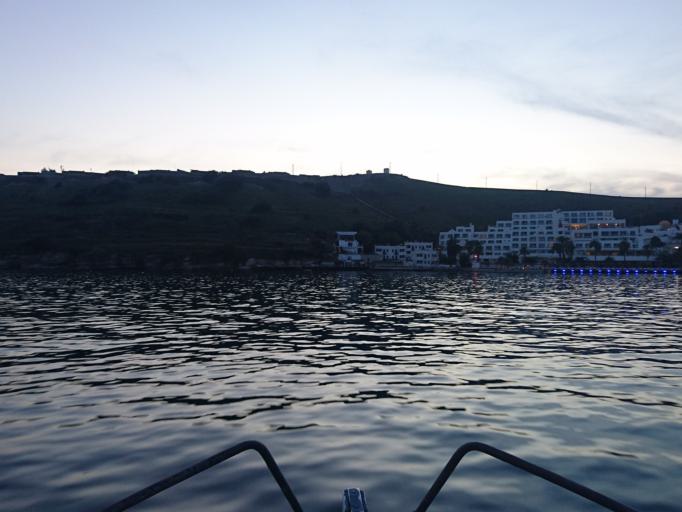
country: TR
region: Mugla
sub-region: Bodrum
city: Bodrum
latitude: 37.0278
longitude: 27.4195
